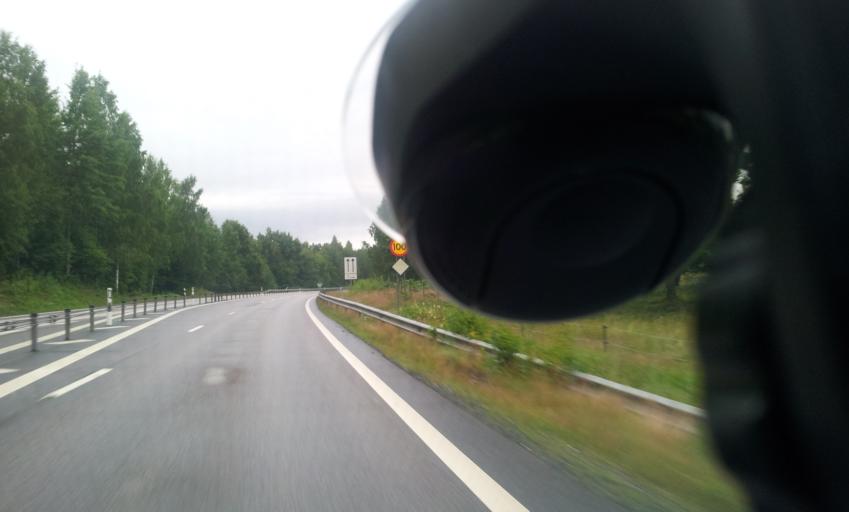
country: SE
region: Kalmar
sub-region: Vasterviks Kommun
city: Forserum
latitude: 58.0755
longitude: 16.5179
